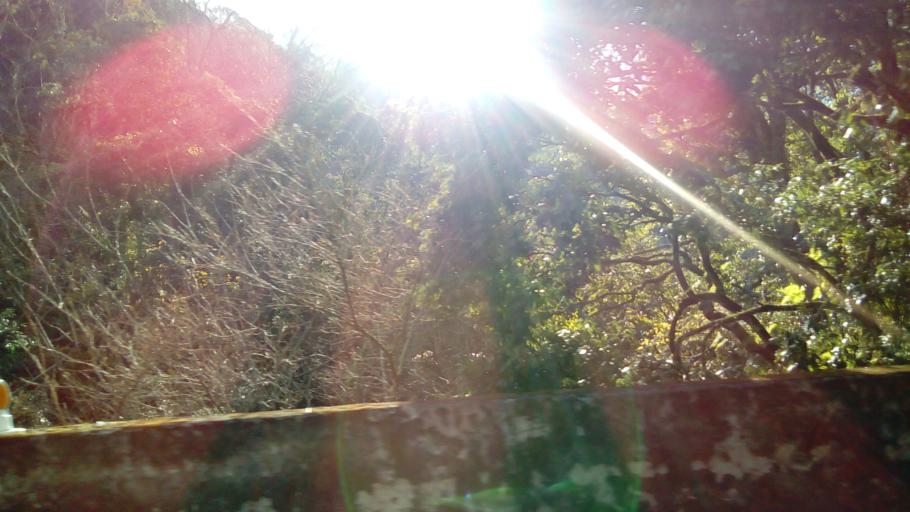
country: TW
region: Taiwan
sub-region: Hualien
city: Hualian
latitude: 24.3447
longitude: 121.3153
